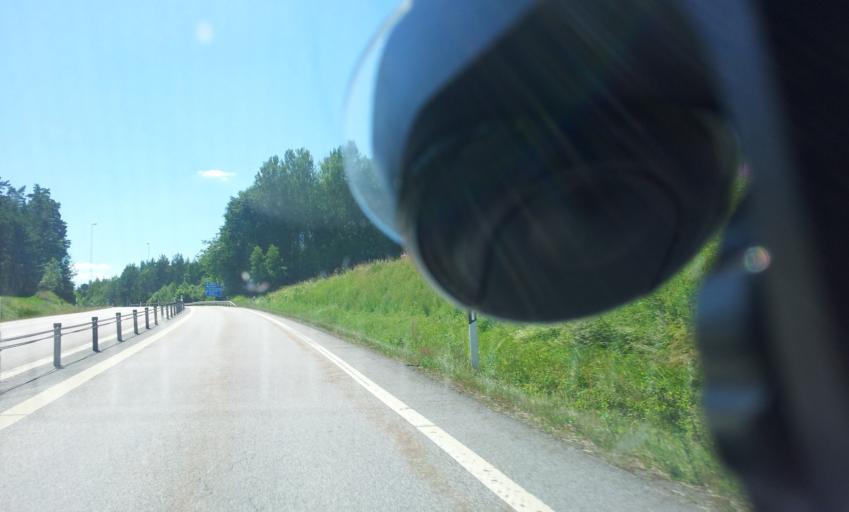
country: SE
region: Kalmar
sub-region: Vasterviks Kommun
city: Forserum
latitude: 58.0057
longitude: 16.4903
